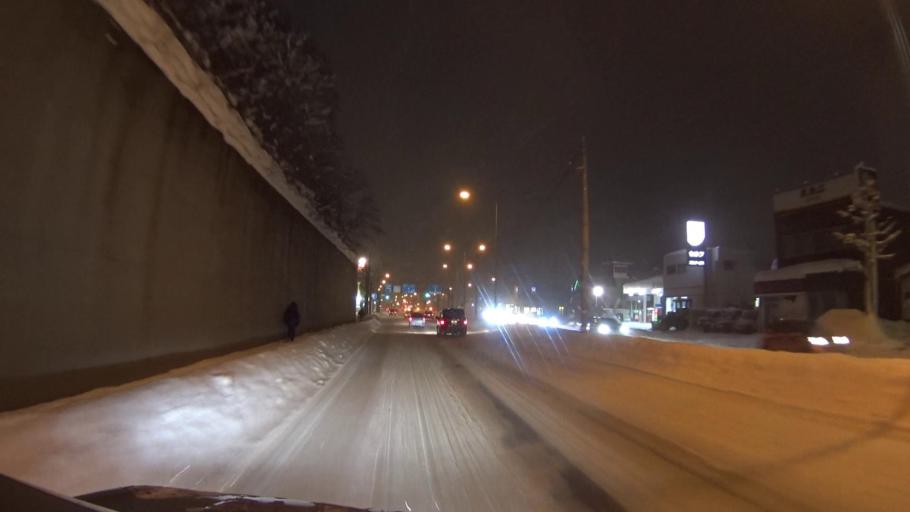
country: JP
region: Hokkaido
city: Otaru
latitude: 43.1897
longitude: 141.0092
